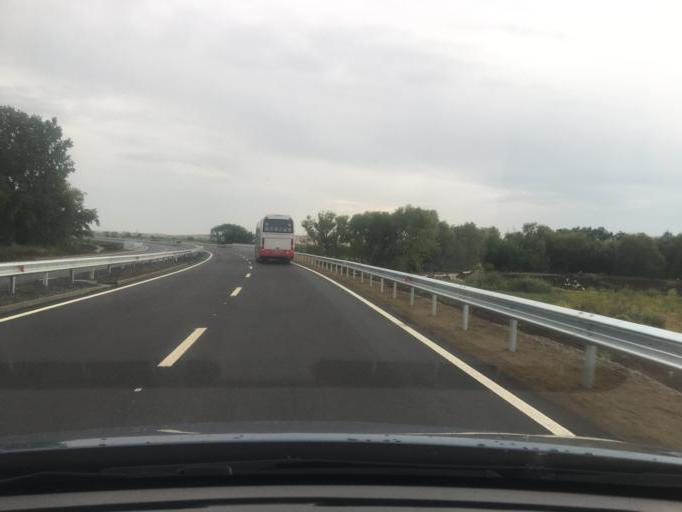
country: BG
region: Burgas
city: Aheloy
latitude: 42.6536
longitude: 27.6394
